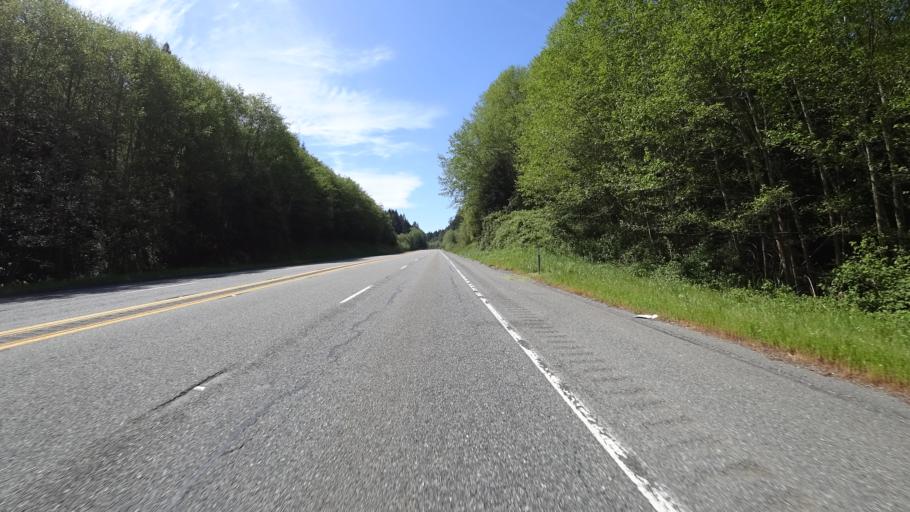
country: US
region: California
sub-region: Del Norte County
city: Bertsch-Oceanview
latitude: 41.4431
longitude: -124.0204
